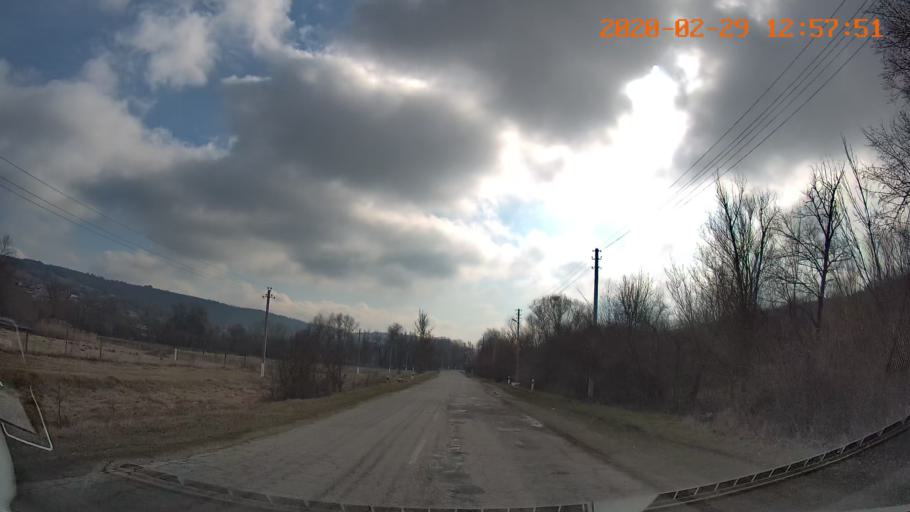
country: MD
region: Telenesti
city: Camenca
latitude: 48.0739
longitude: 28.7171
